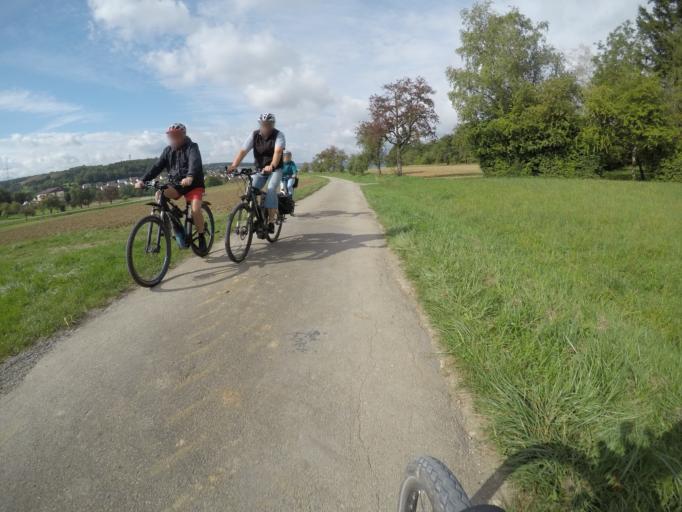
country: DE
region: Baden-Wuerttemberg
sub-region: Karlsruhe Region
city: Althengstett
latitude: 48.7304
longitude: 8.8081
